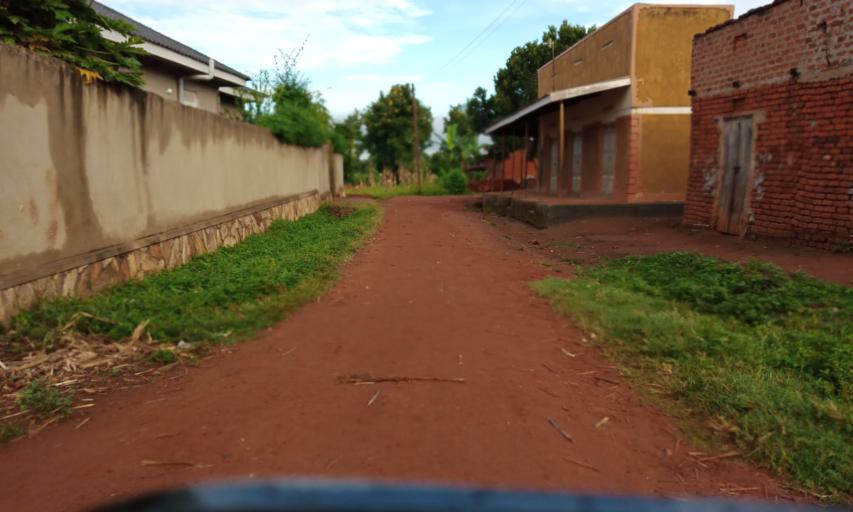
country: UG
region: Eastern Region
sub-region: Mbale District
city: Mbale
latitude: 1.1477
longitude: 34.1675
